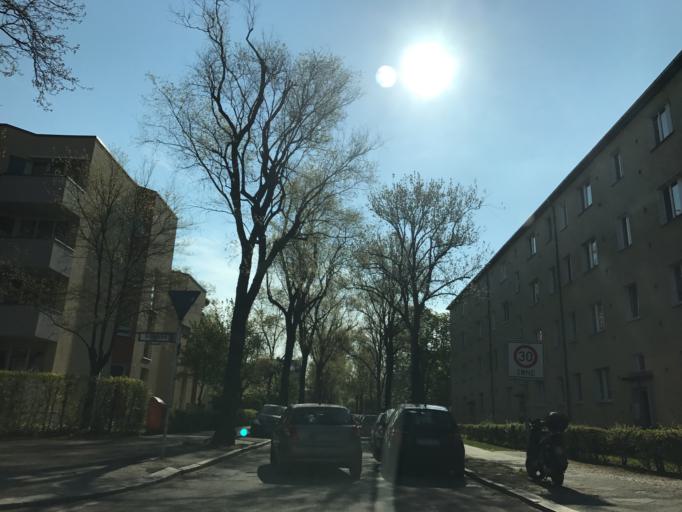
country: DE
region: Berlin
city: Westend
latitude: 52.5189
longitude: 13.2618
